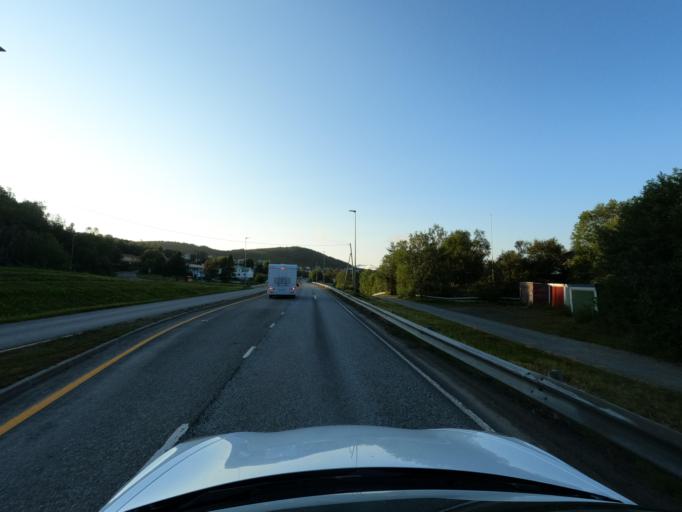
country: NO
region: Troms
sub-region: Harstad
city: Harstad
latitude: 68.7657
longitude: 16.5602
